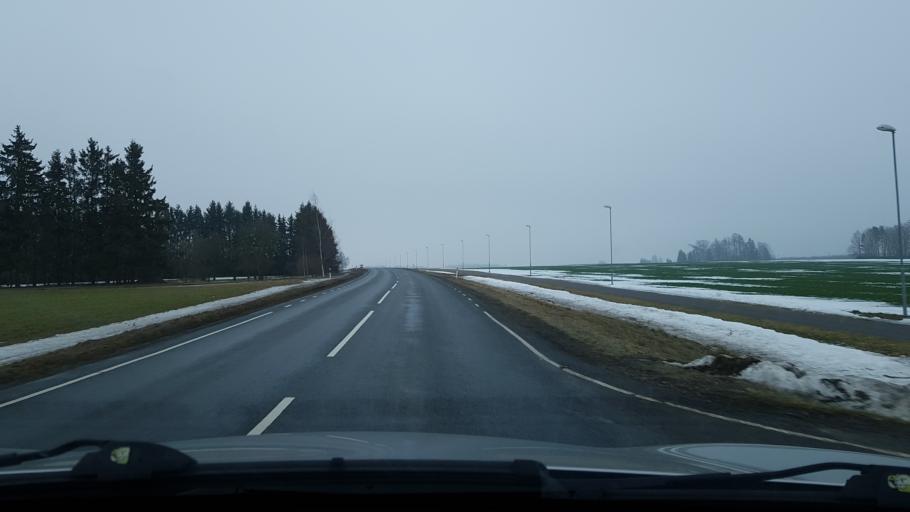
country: EE
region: Valgamaa
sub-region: Torva linn
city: Torva
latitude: 58.2217
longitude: 25.8966
